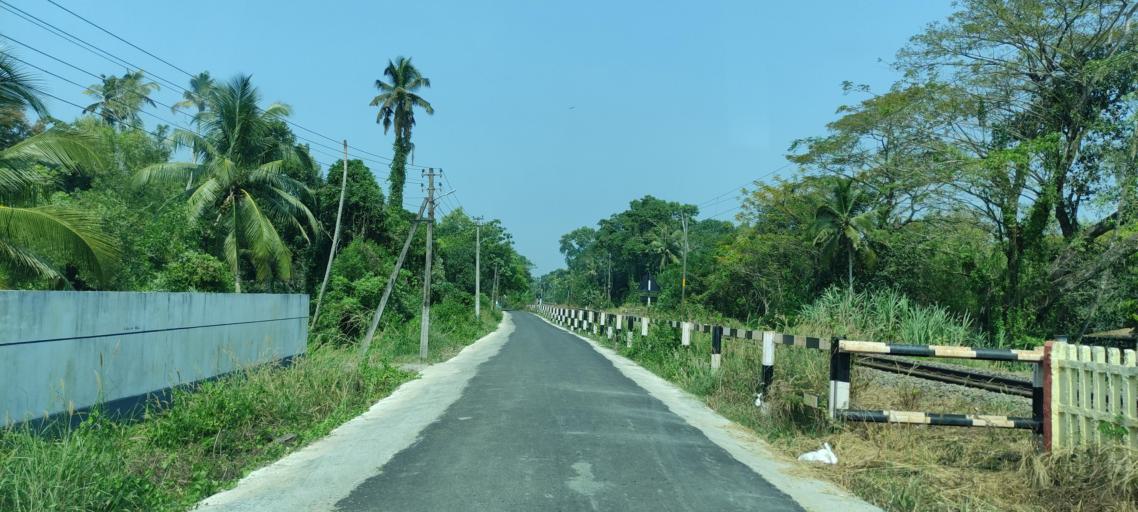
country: IN
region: Kerala
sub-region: Alappuzha
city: Alleppey
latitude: 9.5352
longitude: 76.3210
